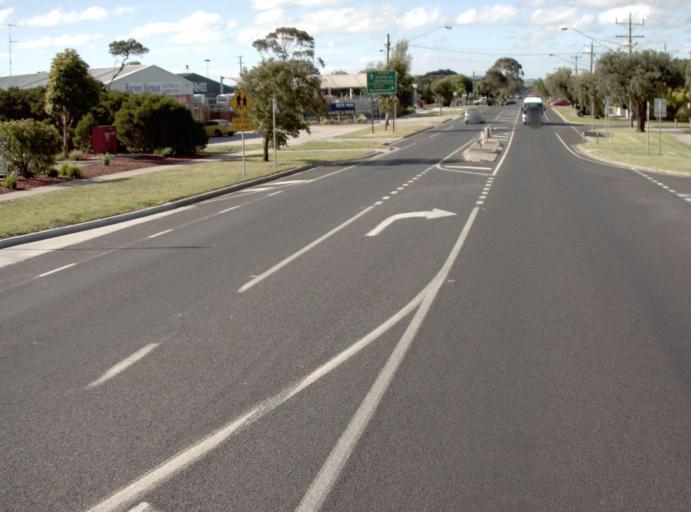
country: AU
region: Victoria
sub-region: Bass Coast
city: North Wonthaggi
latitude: -38.6042
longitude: 145.5935
